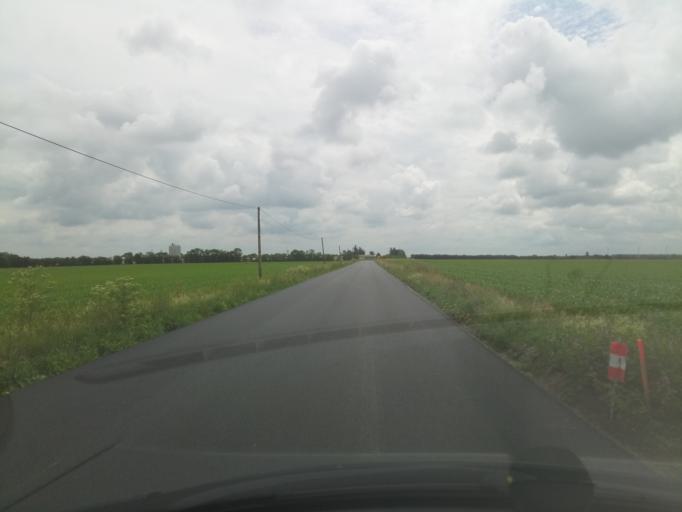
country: FR
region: Poitou-Charentes
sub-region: Departement de la Charente-Maritime
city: Saint-Jean-de-Liversay
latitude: 46.2702
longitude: -0.8926
